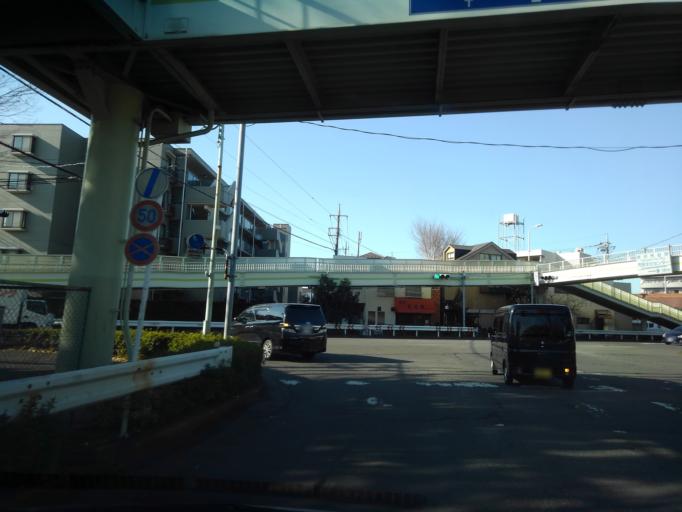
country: JP
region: Saitama
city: Tokorozawa
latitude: 35.8067
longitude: 139.4610
